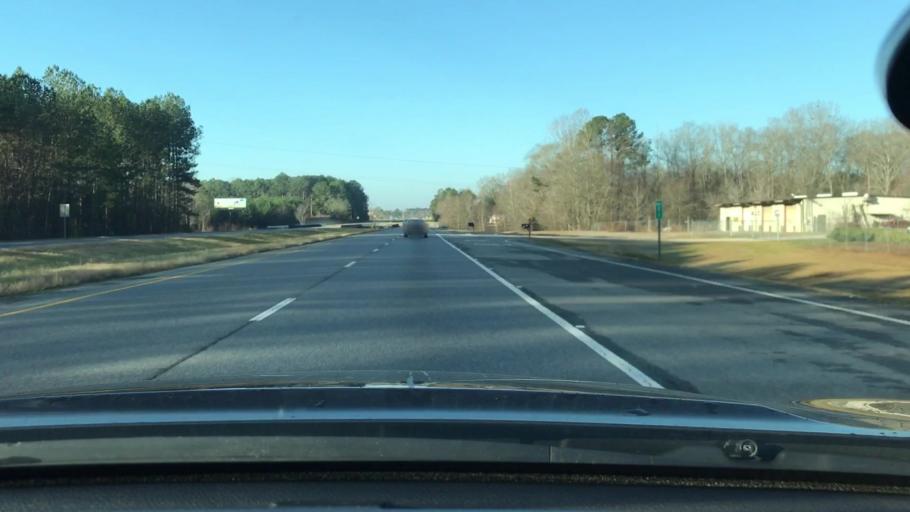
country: US
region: Alabama
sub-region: Shelby County
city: Westover
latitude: 33.3539
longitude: -86.5236
